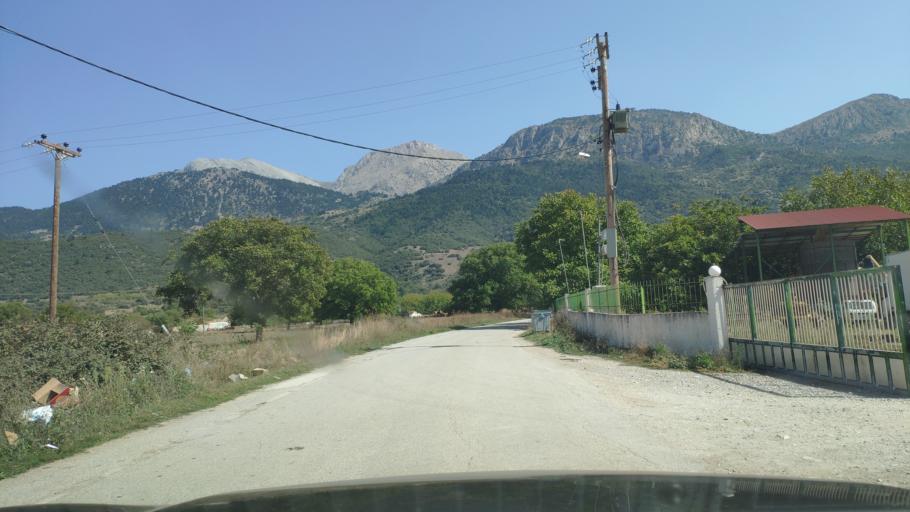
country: GR
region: West Greece
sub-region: Nomos Achaias
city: Kalavryta
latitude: 37.9082
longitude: 22.3209
